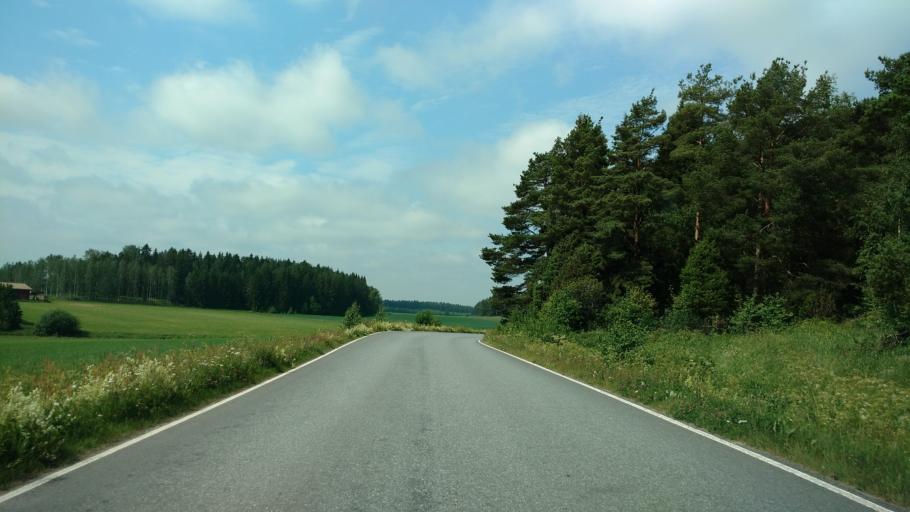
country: FI
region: Haeme
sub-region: Forssa
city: Ypaejae
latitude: 60.7881
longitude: 23.3722
